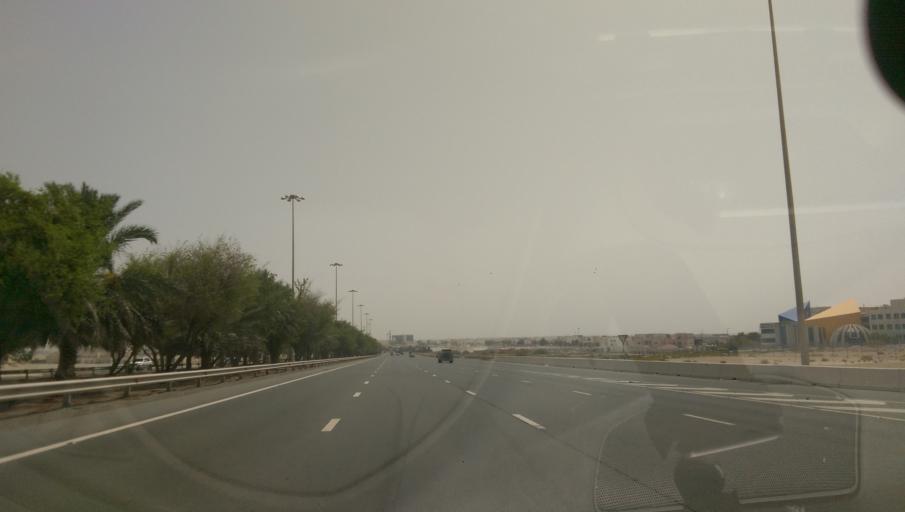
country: AE
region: Abu Dhabi
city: Abu Dhabi
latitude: 24.3279
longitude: 54.6245
